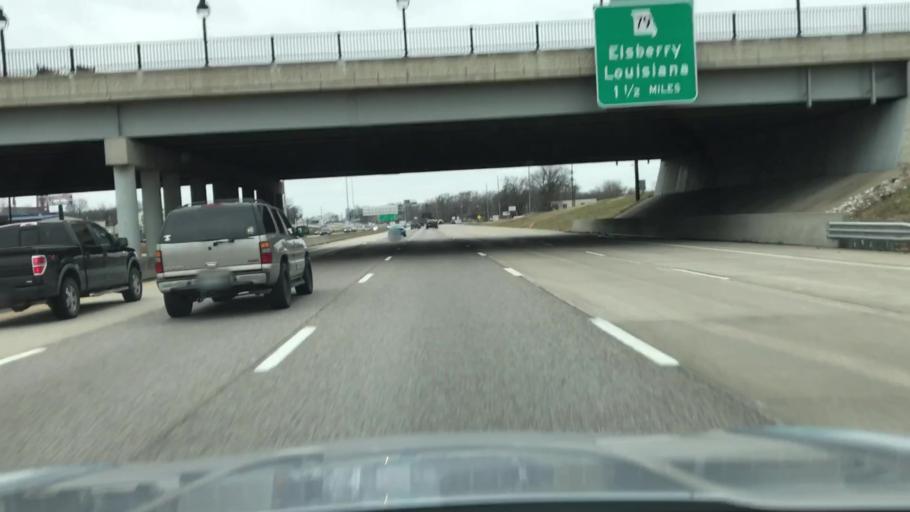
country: US
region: Missouri
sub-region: Saint Charles County
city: Saint Peters
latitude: 38.7999
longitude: -90.6199
